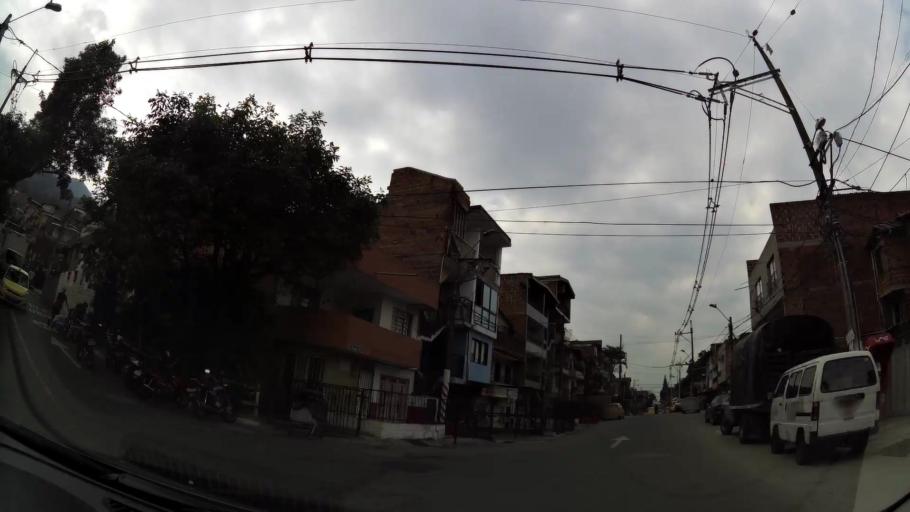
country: CO
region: Antioquia
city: Medellin
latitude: 6.2808
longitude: -75.5538
